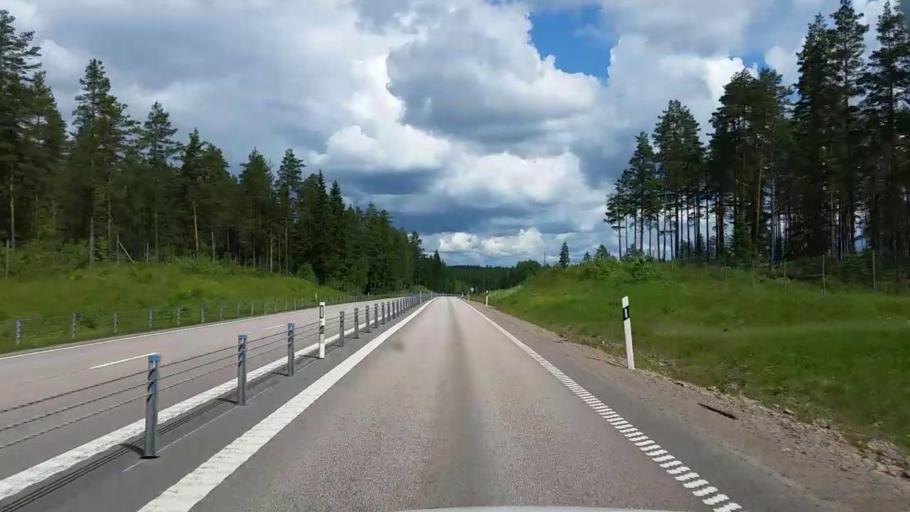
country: SE
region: Vaestmanland
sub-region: Norbergs Kommun
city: Norberg
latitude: 60.0864
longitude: 15.9868
